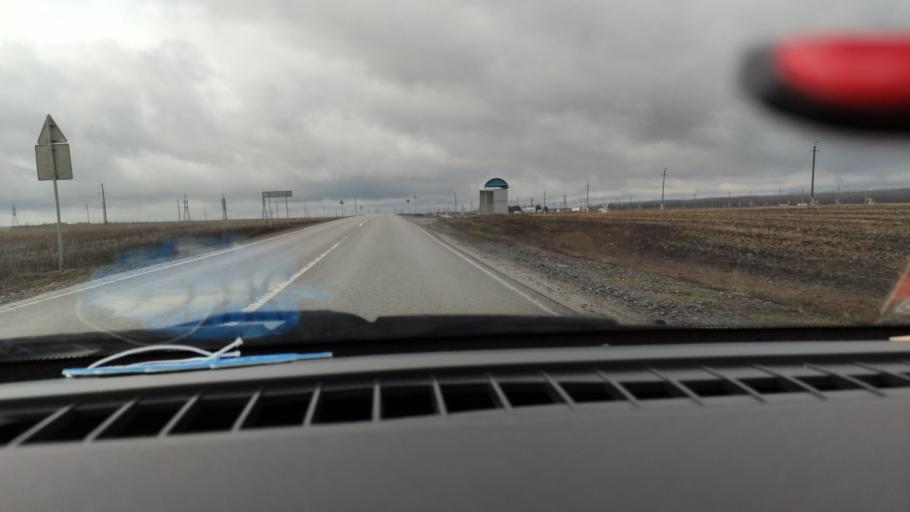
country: RU
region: Tatarstan
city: Nurlat
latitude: 54.4811
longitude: 50.8455
